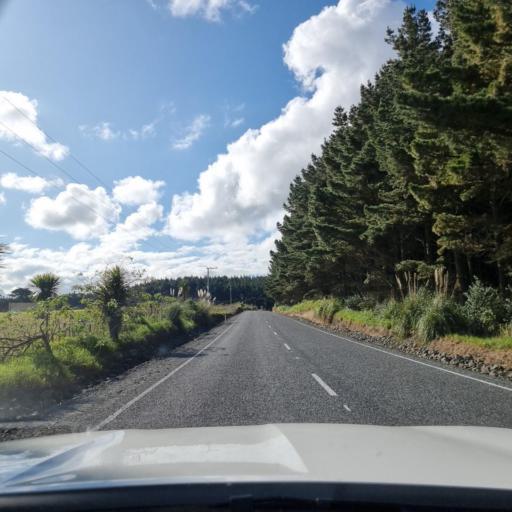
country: NZ
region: Northland
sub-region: Kaipara District
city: Dargaville
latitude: -36.2503
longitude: 174.0430
